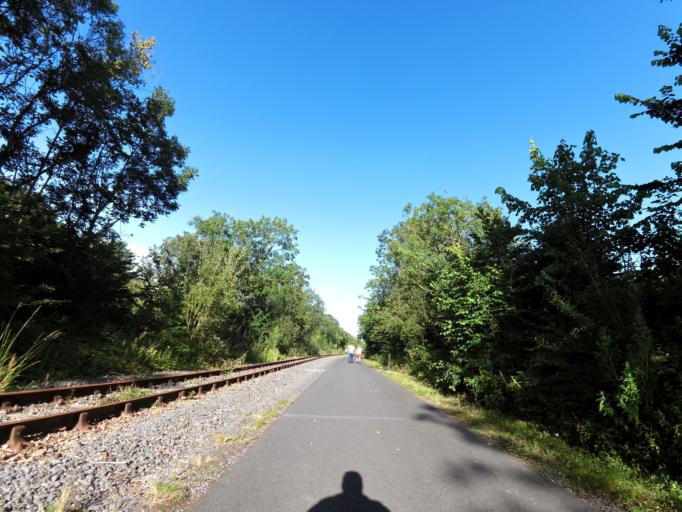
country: IE
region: Munster
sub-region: Waterford
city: Waterford
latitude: 52.2736
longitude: -7.1543
